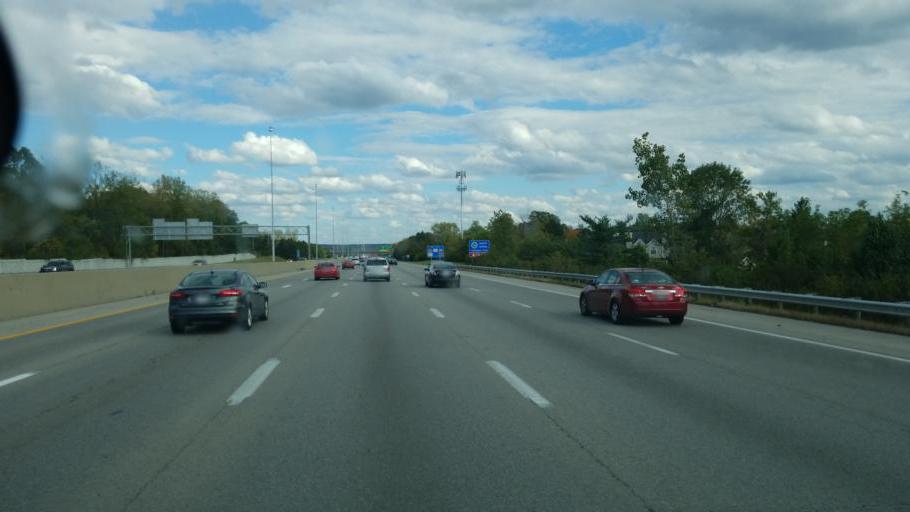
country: US
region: Ohio
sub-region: Franklin County
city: Minerva Park
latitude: 40.1093
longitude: -82.9693
